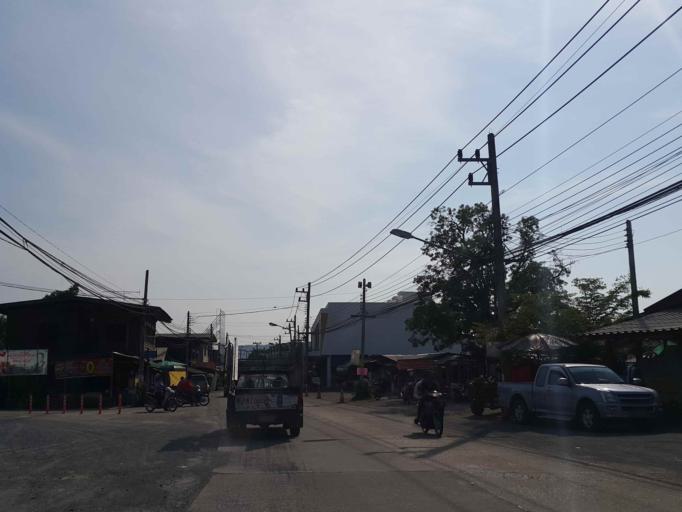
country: TH
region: Sukhothai
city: Thung Saliam
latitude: 17.3197
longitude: 99.5587
